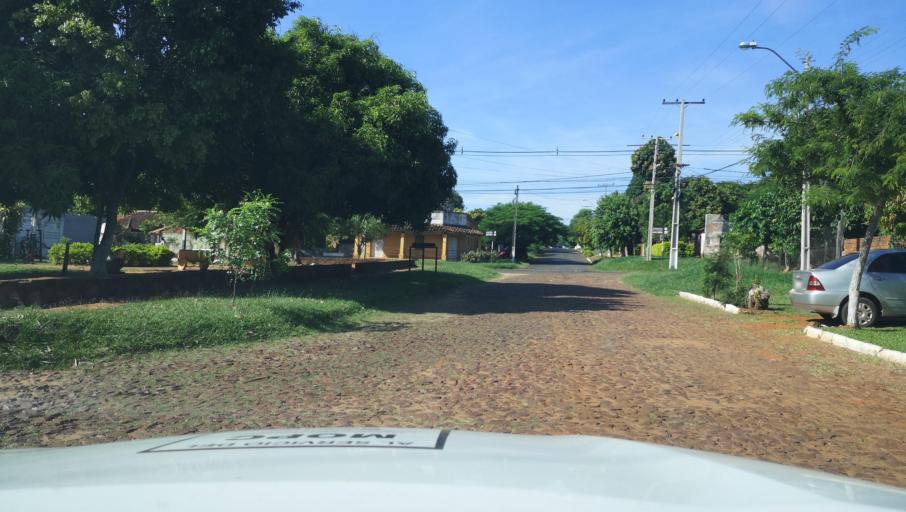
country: PY
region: Misiones
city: Santa Maria
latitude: -26.8850
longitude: -57.0165
